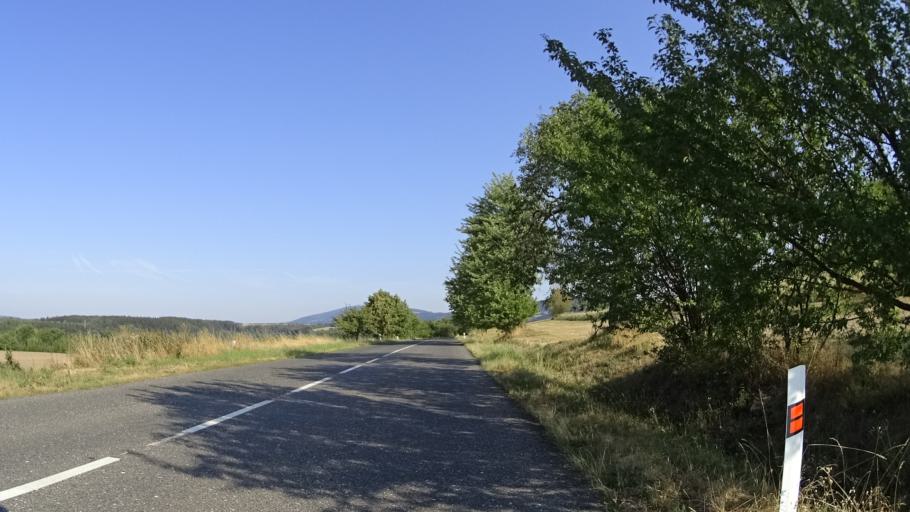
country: CZ
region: Liberecky
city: Hodkovice nad Mohelkou
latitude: 50.6439
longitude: 15.1077
